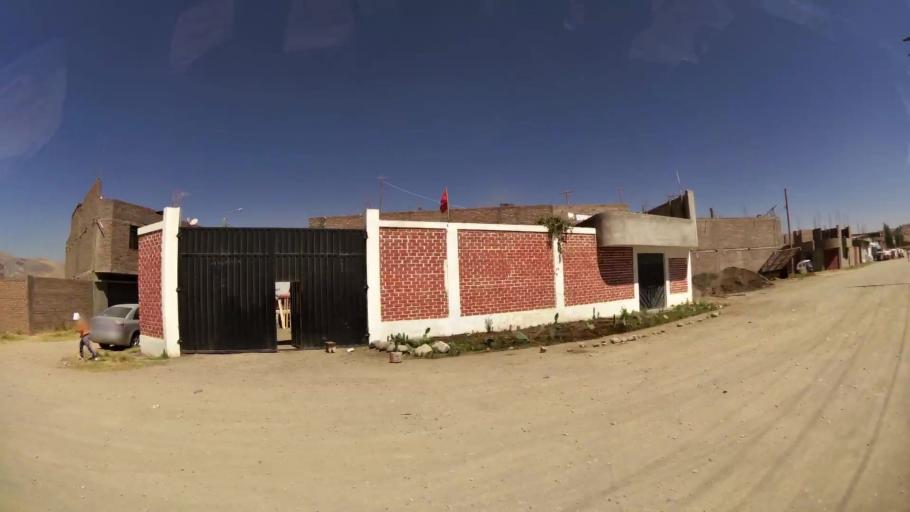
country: PE
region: Junin
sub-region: Provincia de Jauja
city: Jauja
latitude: -11.7785
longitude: -75.4904
